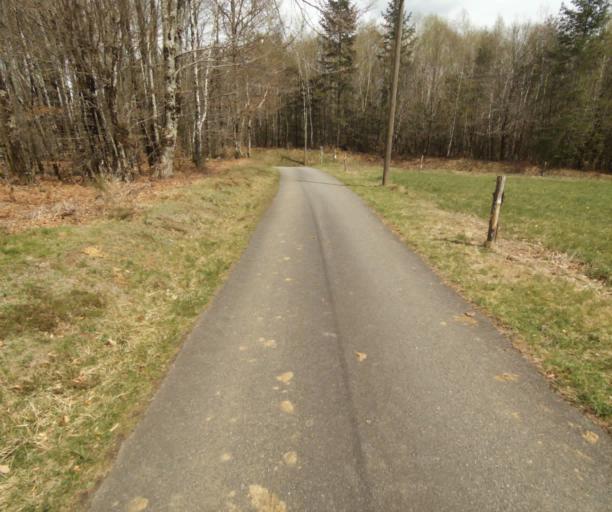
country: FR
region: Limousin
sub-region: Departement de la Correze
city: Argentat
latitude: 45.1938
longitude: 1.8890
